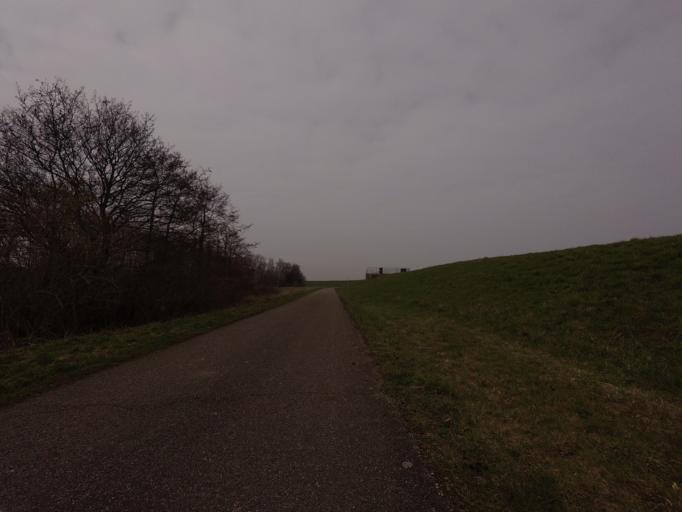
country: NL
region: North Brabant
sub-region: Gemeente Woensdrecht
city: Woensdrecht
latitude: 51.3495
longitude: 4.2274
